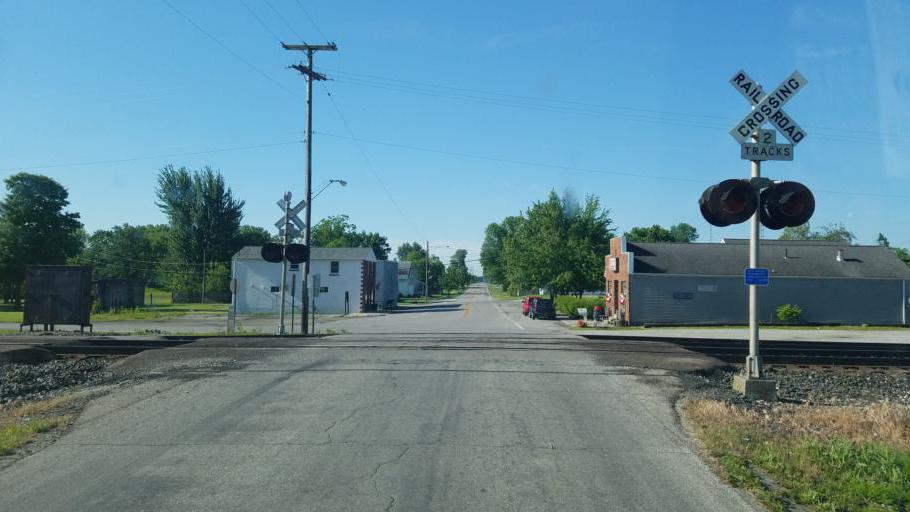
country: US
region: Ohio
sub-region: Union County
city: Richwood
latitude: 40.5861
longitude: -83.3149
